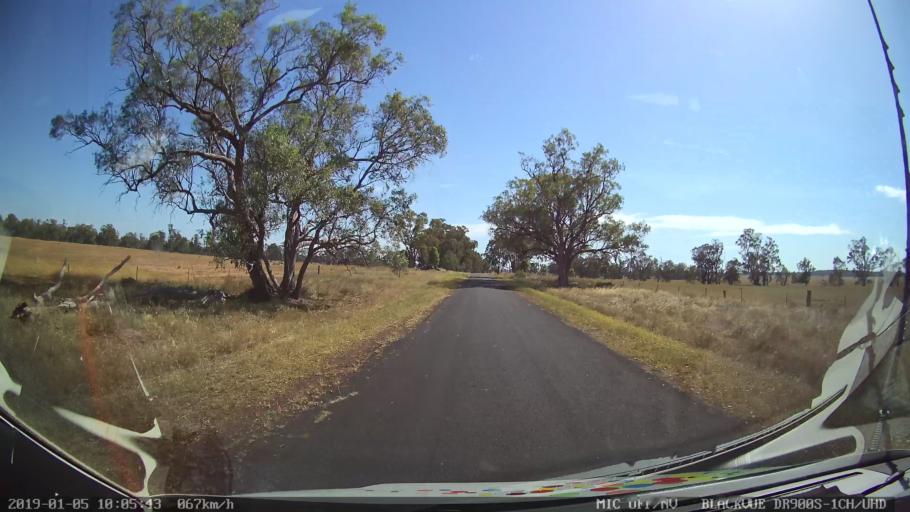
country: AU
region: New South Wales
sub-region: Gilgandra
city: Gilgandra
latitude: -31.6633
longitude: 148.8663
